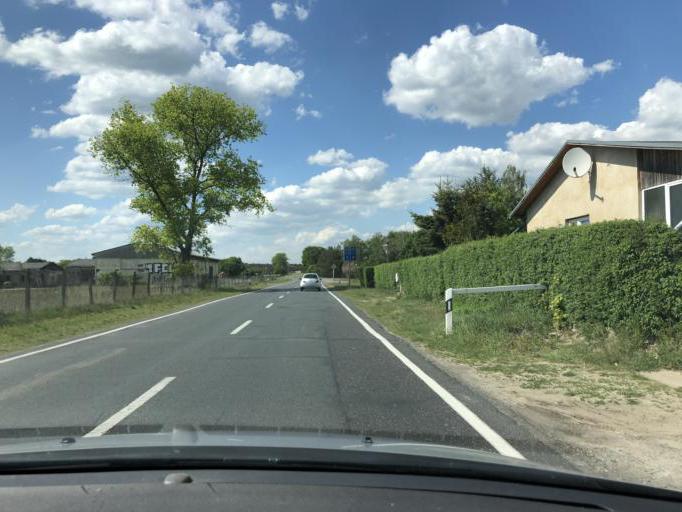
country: DE
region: Brandenburg
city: Spreenhagen
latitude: 52.3396
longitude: 13.8888
